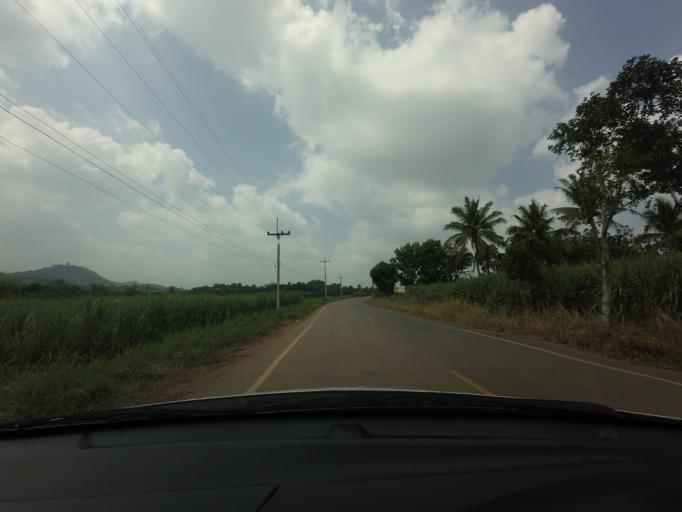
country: TH
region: Nakhon Ratchasima
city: Pak Chong
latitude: 14.5503
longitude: 101.5889
